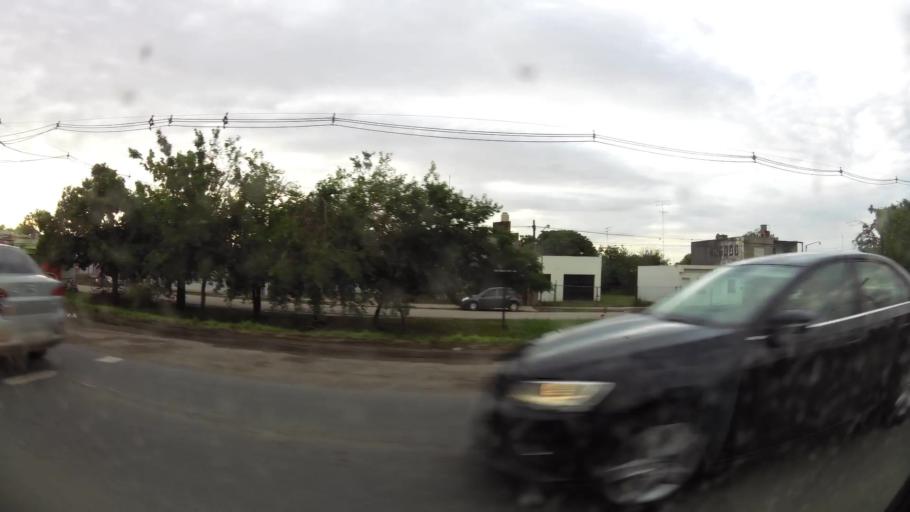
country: AR
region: Buenos Aires
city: San Nicolas de los Arroyos
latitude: -33.3677
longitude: -60.1977
